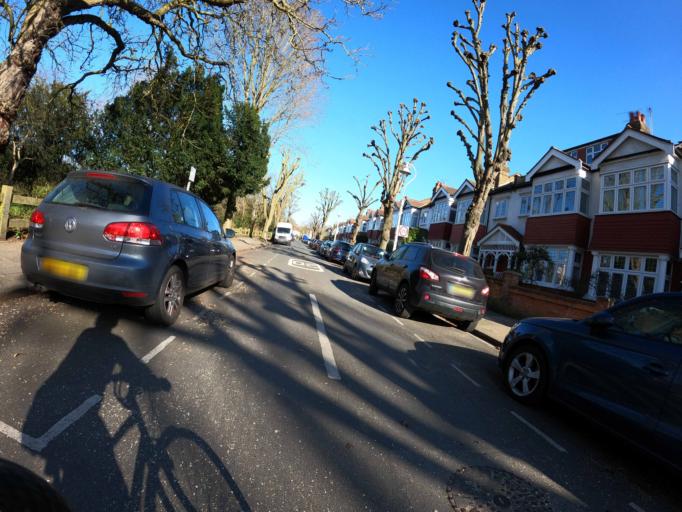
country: GB
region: England
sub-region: Greater London
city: Ealing
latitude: 51.5051
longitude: -0.3091
